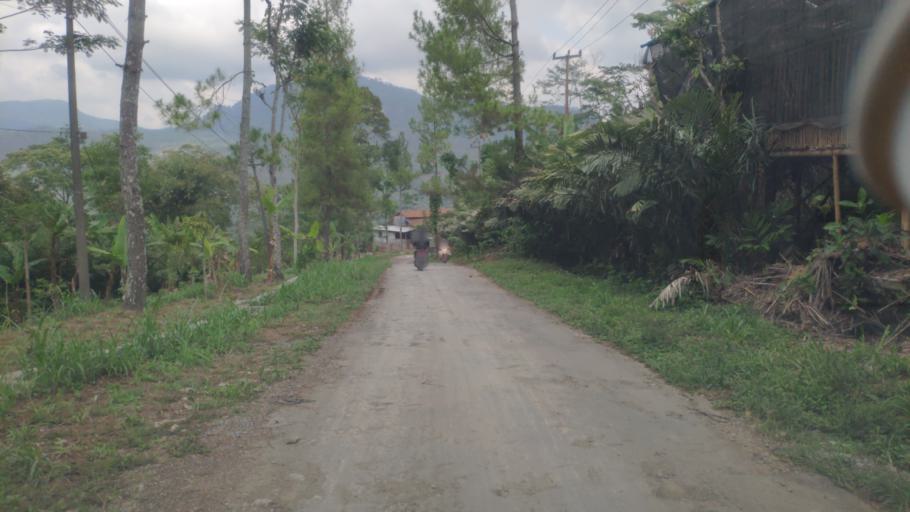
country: ID
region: Central Java
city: Wonosobo
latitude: -7.3177
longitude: 109.7802
